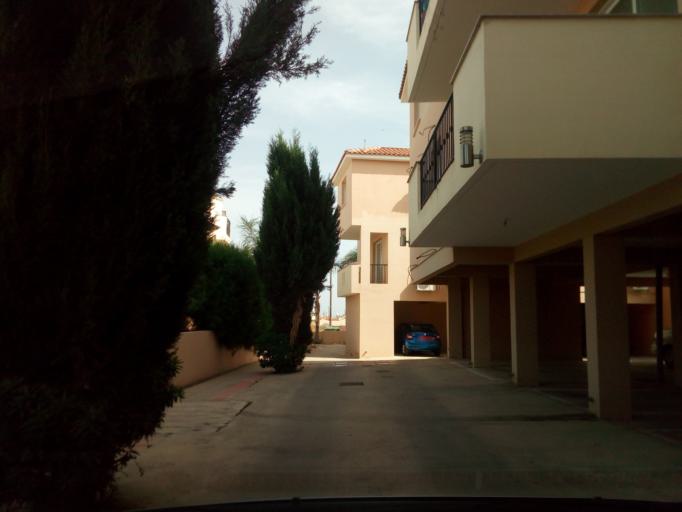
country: CY
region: Larnaka
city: Kiti
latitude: 34.8445
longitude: 33.5689
